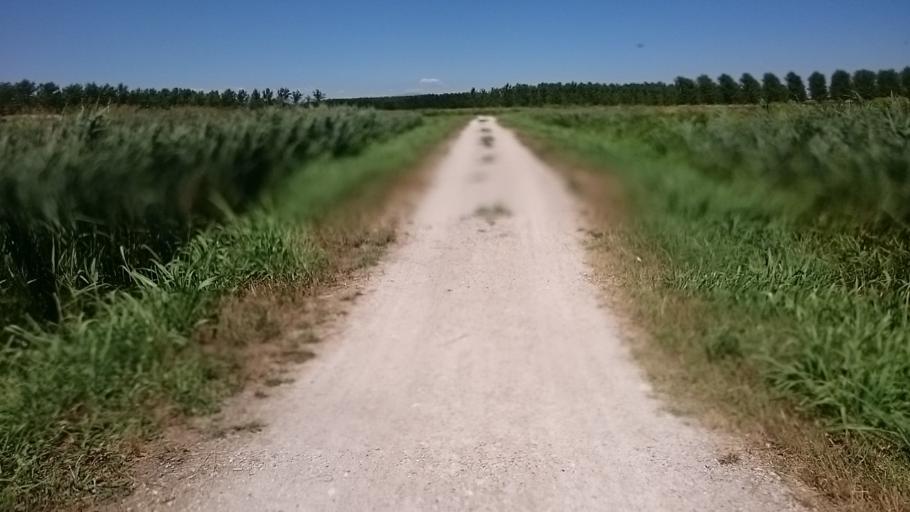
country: IT
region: Veneto
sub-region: Provincia di Padova
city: Borgoricco-San Michele delle Badesse-Sant'Eufemia
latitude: 45.5222
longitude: 11.9303
